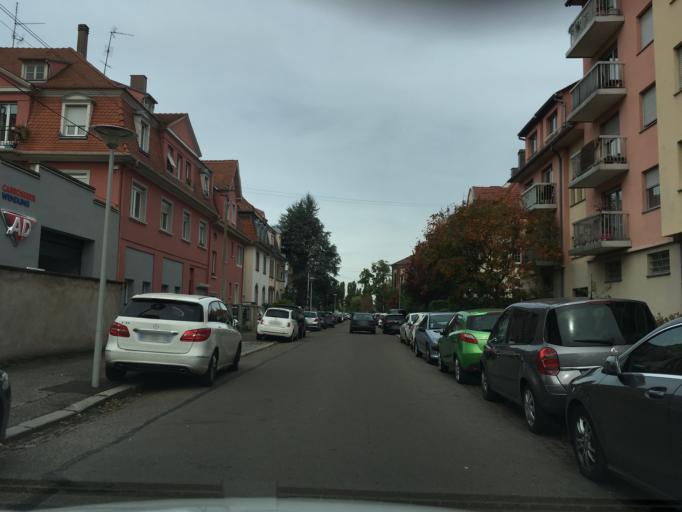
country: FR
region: Alsace
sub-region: Departement du Bas-Rhin
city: Bischheim
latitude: 48.6007
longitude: 7.7809
